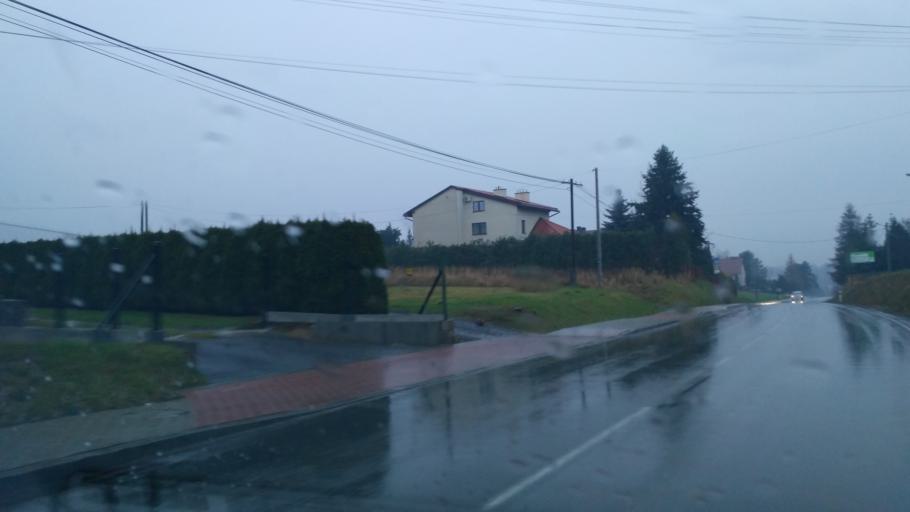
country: PL
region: Subcarpathian Voivodeship
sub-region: Powiat lancucki
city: Krzemienica
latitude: 50.0715
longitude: 22.2011
